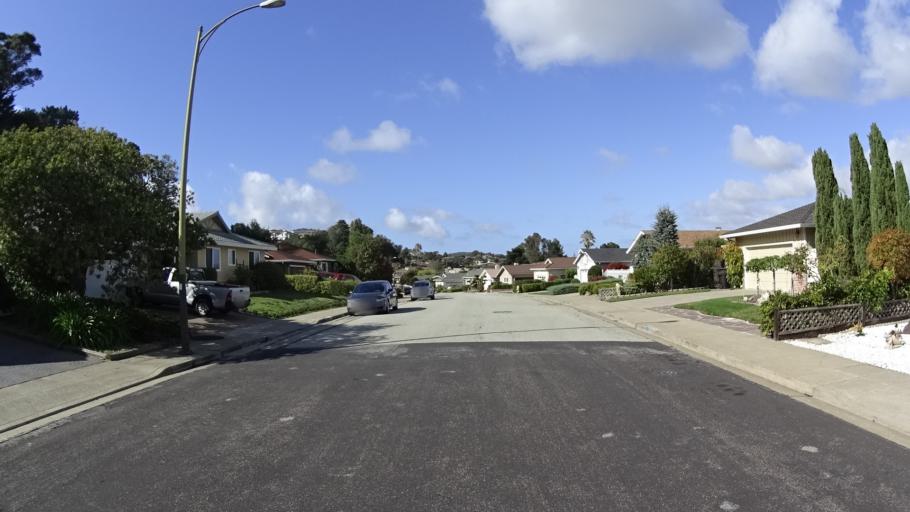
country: US
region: California
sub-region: San Mateo County
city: Millbrae
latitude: 37.5880
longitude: -122.3920
